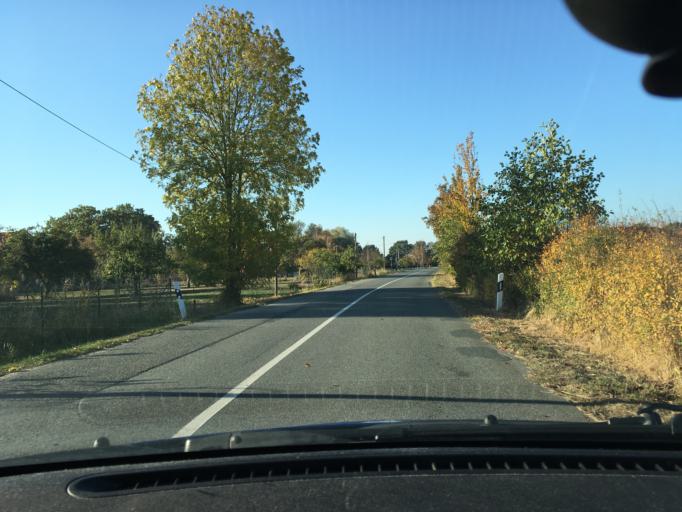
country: DE
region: Lower Saxony
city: Hitzacker
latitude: 53.1550
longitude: 11.0771
